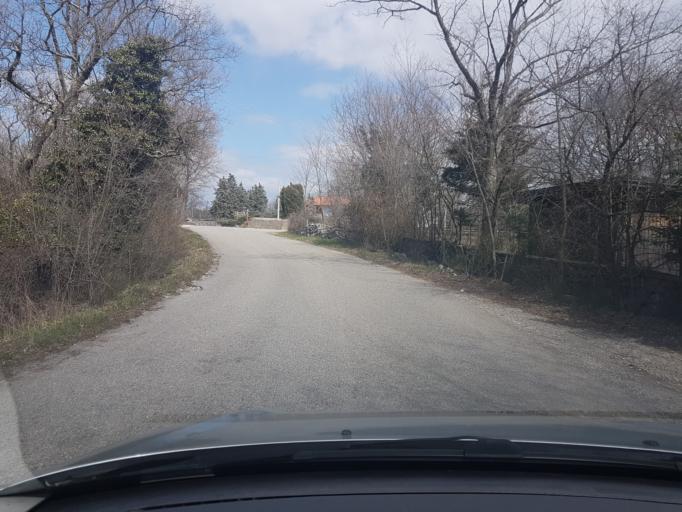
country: IT
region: Friuli Venezia Giulia
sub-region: Provincia di Trieste
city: Santa Croce
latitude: 45.7499
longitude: 13.7164
